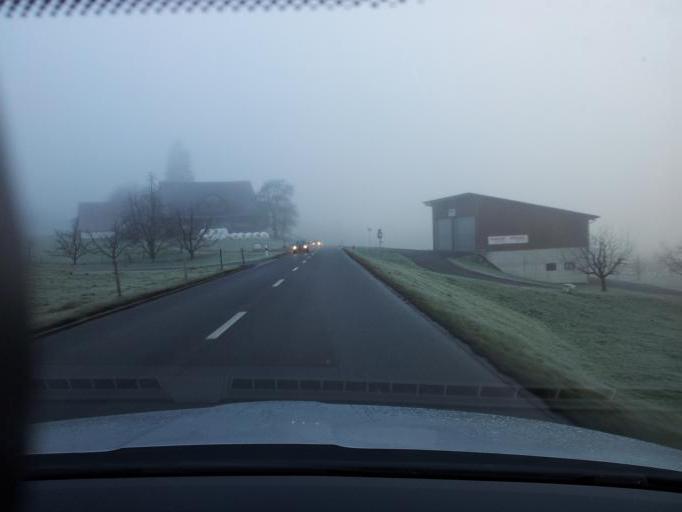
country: CH
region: Lucerne
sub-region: Lucerne-Stadt District
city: Littau
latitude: 47.0403
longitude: 8.2305
